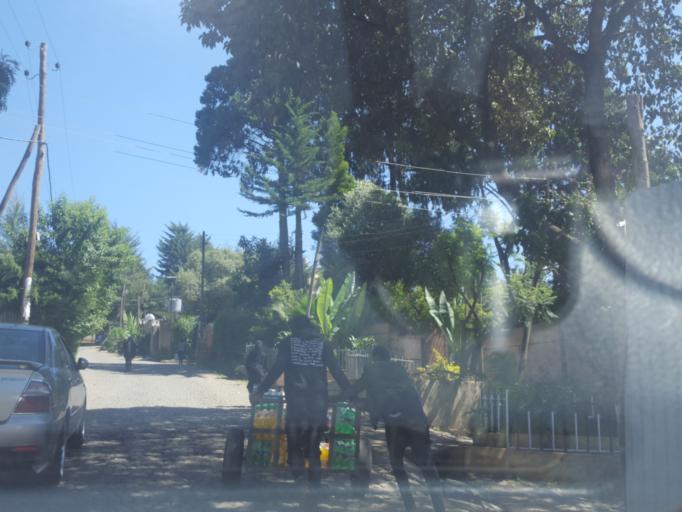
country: ET
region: Adis Abeba
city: Addis Ababa
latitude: 9.0612
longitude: 38.7376
